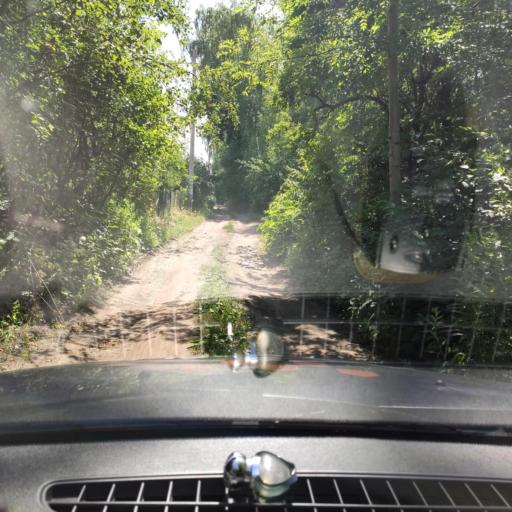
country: RU
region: Voronezj
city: Voronezh
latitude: 51.5989
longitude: 39.1547
